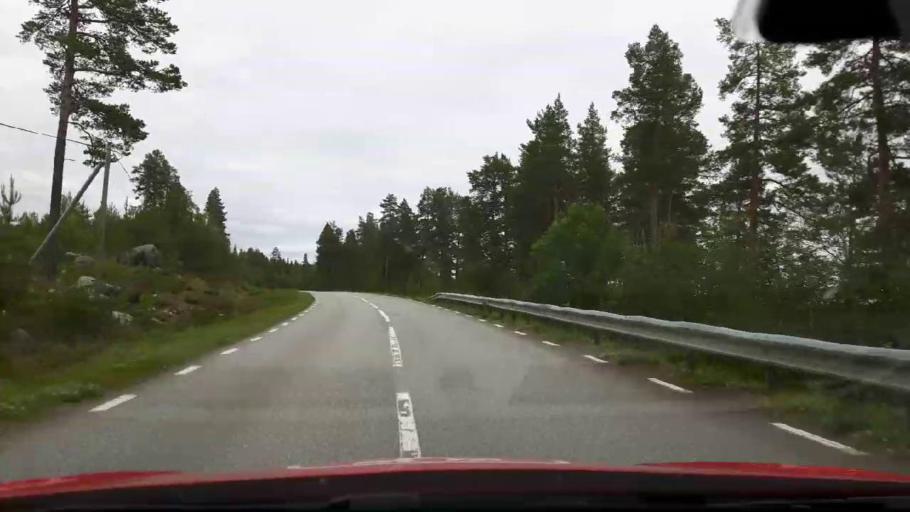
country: SE
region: Jaemtland
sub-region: Stroemsunds Kommun
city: Stroemsund
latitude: 63.3734
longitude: 15.6963
